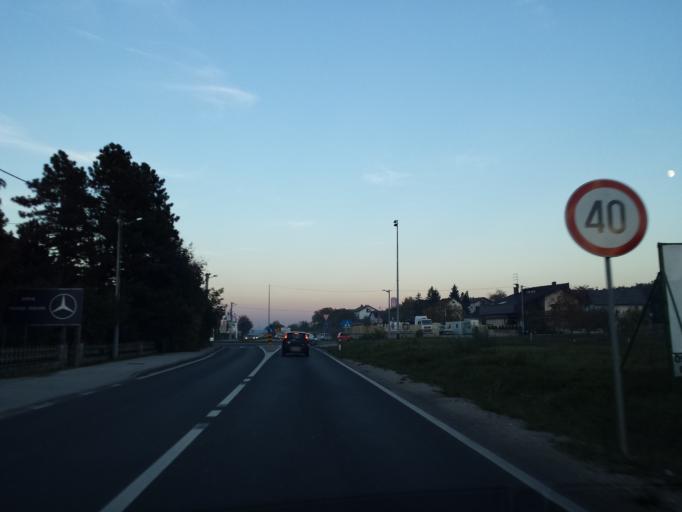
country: HR
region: Zagrebacka
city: Kerestinec
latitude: 45.7974
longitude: 15.7670
